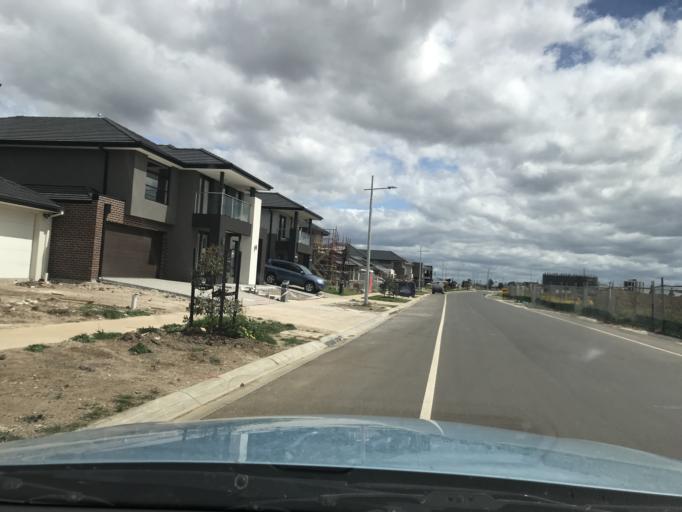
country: AU
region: Victoria
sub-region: Wyndham
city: Williams Landing
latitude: -37.8659
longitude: 144.7530
